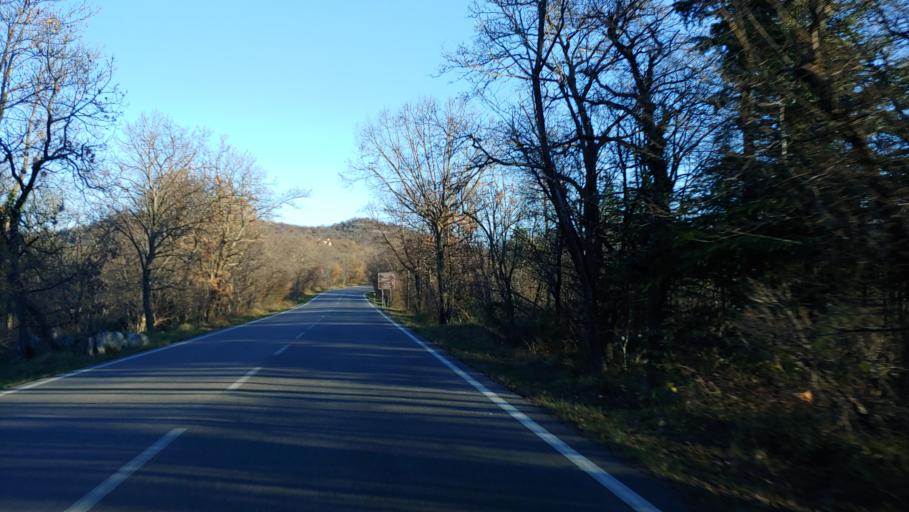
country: IT
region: Friuli Venezia Giulia
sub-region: Provincia di Trieste
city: Zolla
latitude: 45.7058
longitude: 13.8015
